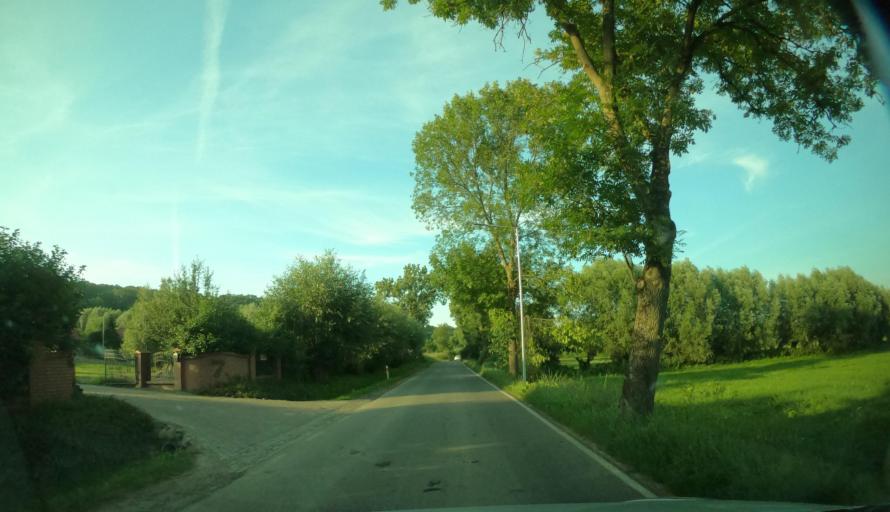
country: PL
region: Kujawsko-Pomorskie
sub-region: Bydgoszcz
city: Fordon
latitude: 53.2213
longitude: 18.1886
